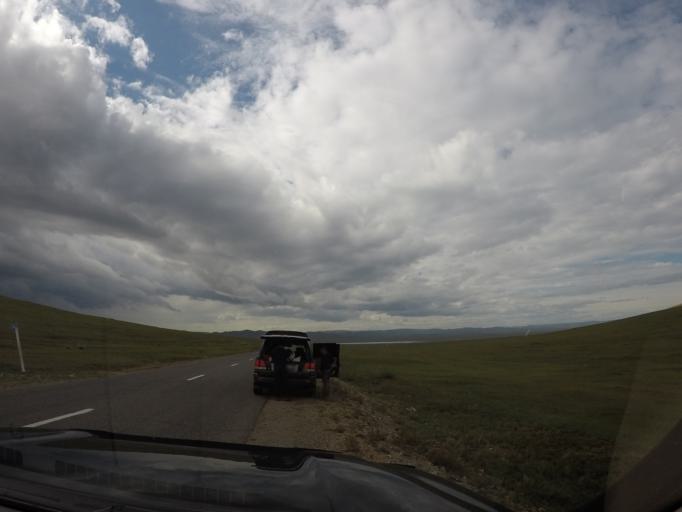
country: MN
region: Hentiy
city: Avraga
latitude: 47.4711
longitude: 109.5304
